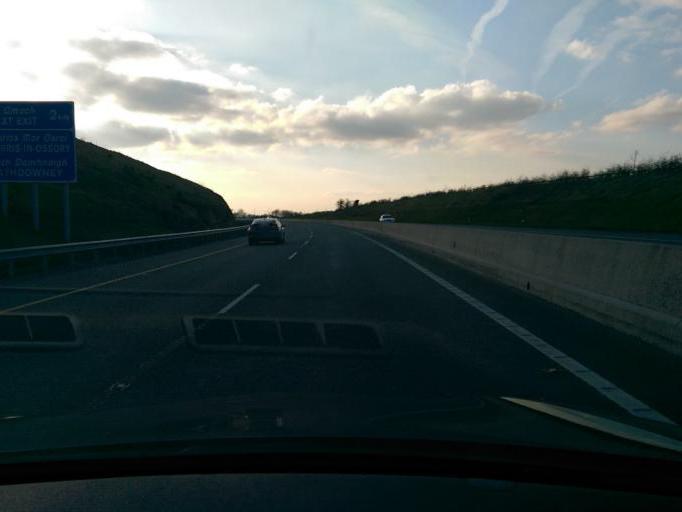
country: IE
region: Leinster
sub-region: Laois
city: Rathdowney
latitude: 52.9263
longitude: -7.5901
